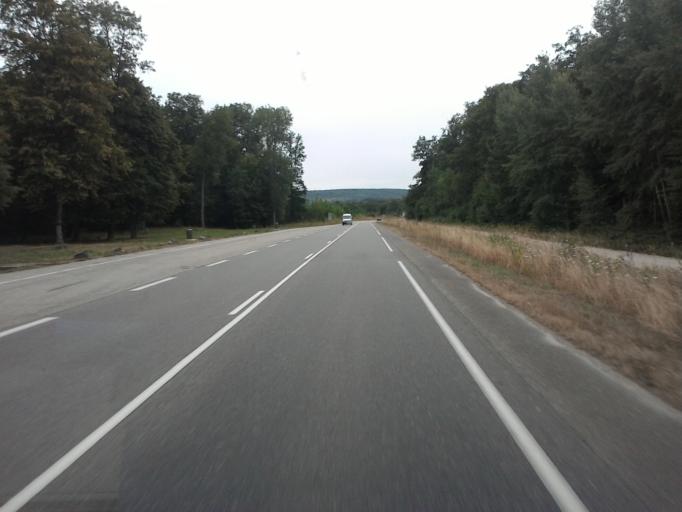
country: FR
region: Lorraine
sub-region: Departement de Meurthe-et-Moselle
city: Pont-Saint-Vincent
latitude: 48.5924
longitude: 6.1107
